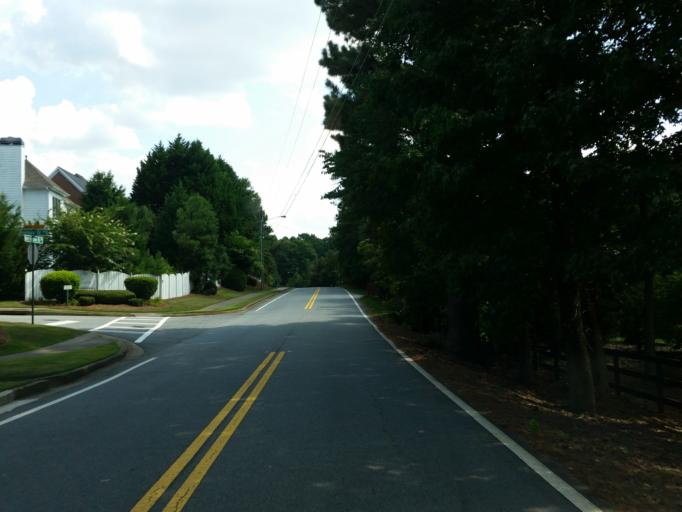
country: US
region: Georgia
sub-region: Fulton County
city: Roswell
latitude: 34.0324
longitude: -84.4421
